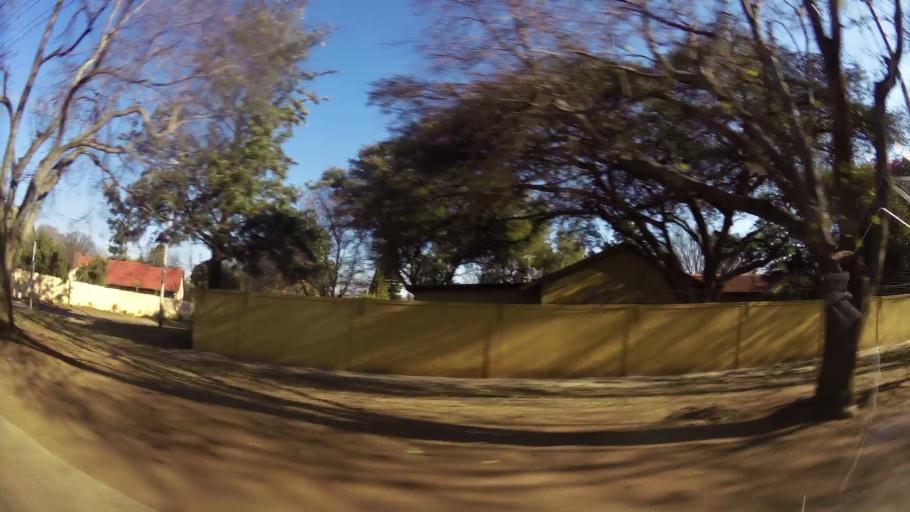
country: ZA
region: Gauteng
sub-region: City of Tshwane Metropolitan Municipality
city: Centurion
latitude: -25.8622
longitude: 28.1422
